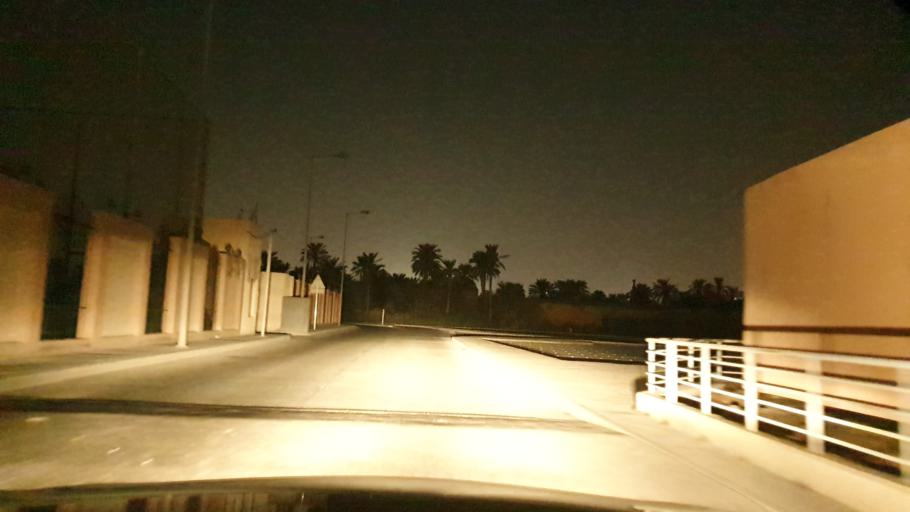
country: BH
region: Manama
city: Jidd Hafs
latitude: 26.1987
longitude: 50.5481
